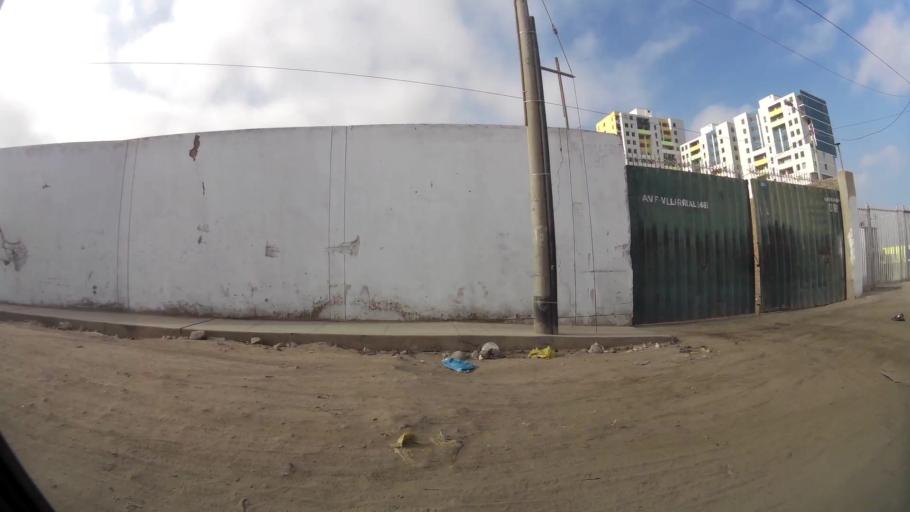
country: PE
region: La Libertad
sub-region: Provincia de Trujillo
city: La Esperanza
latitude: -8.0917
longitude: -79.0349
